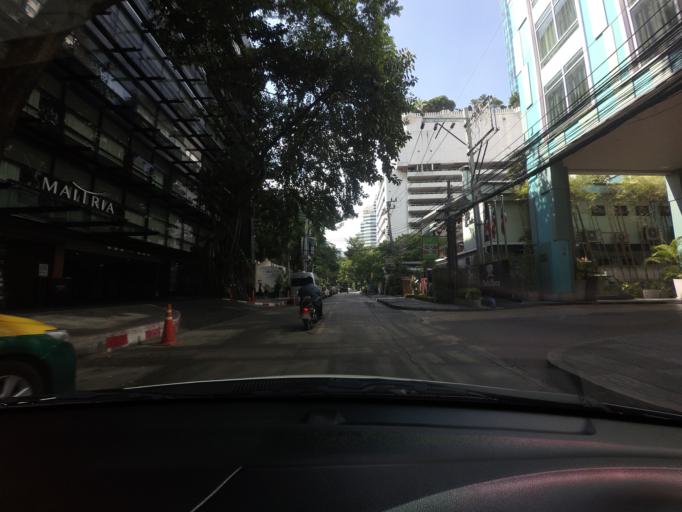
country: TH
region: Bangkok
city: Khlong Toei
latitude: 13.7340
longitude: 100.5625
